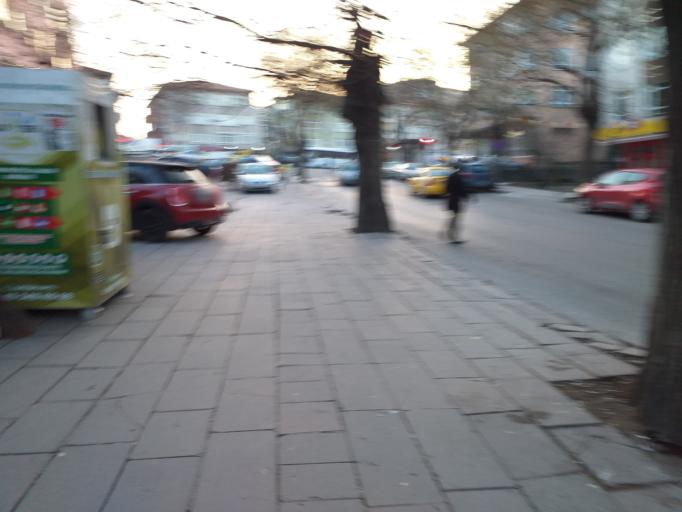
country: TR
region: Ankara
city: Ankara
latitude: 39.9799
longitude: 32.8359
